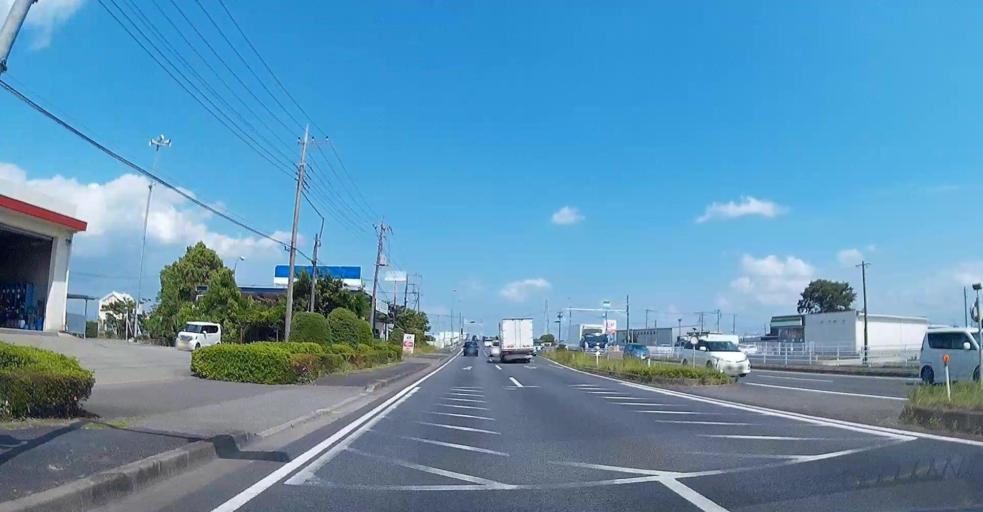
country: JP
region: Saitama
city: Kasukabe
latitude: 35.9920
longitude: 139.7731
